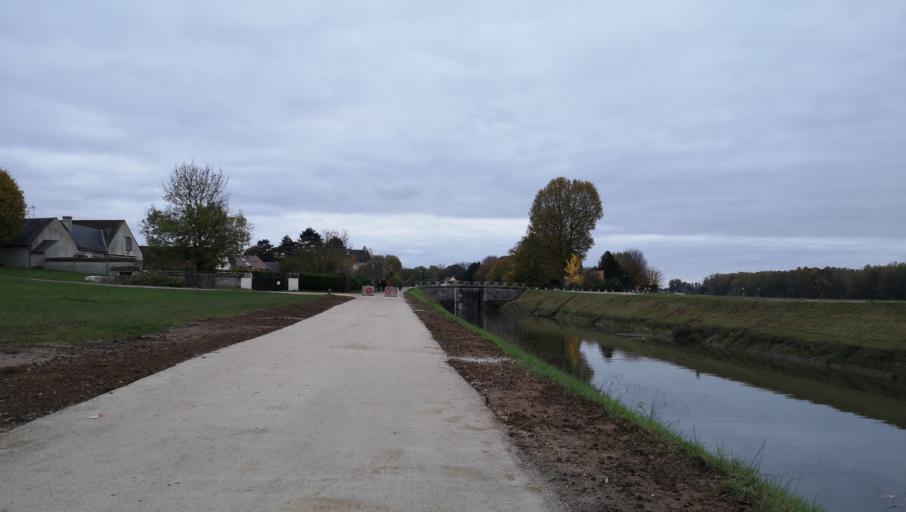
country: FR
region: Centre
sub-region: Departement du Loiret
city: Saint-Jean-de-Braye
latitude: 47.9016
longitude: 1.9827
